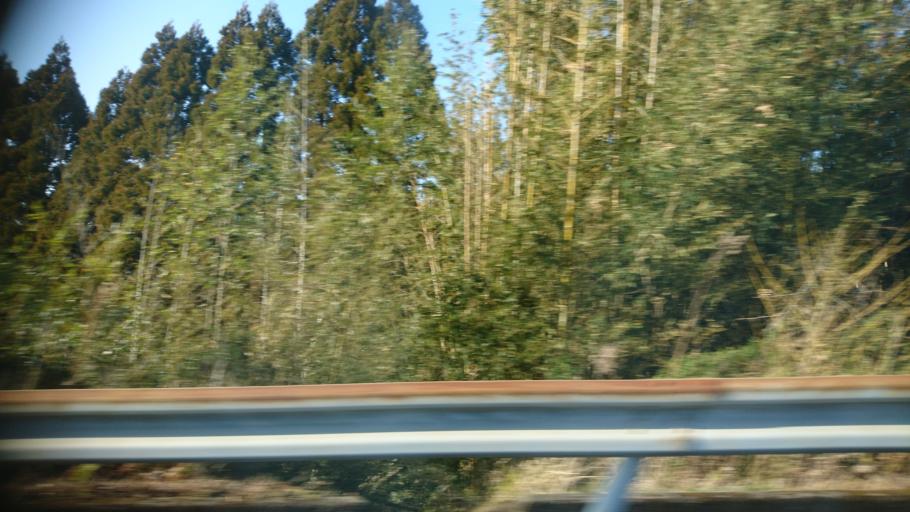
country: JP
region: Miyazaki
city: Kobayashi
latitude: 32.0267
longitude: 130.8583
